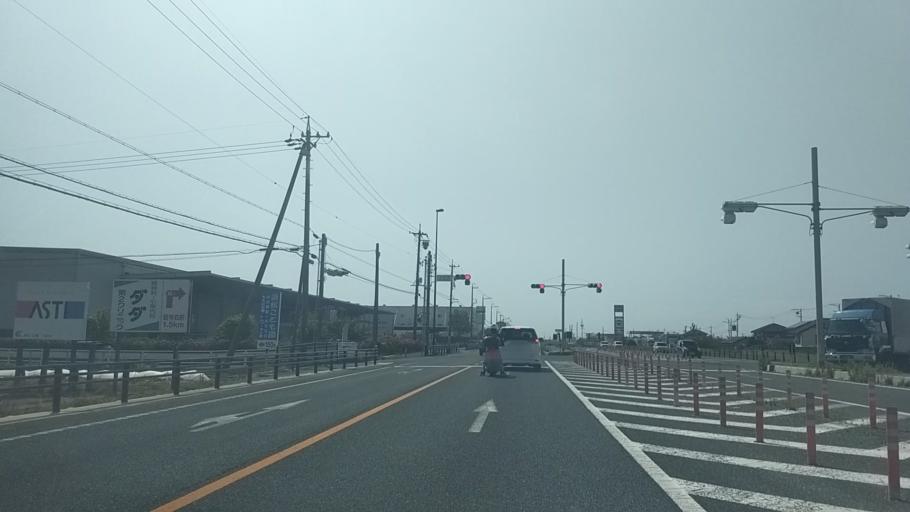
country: JP
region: Shizuoka
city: Hamamatsu
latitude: 34.6706
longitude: 137.7163
